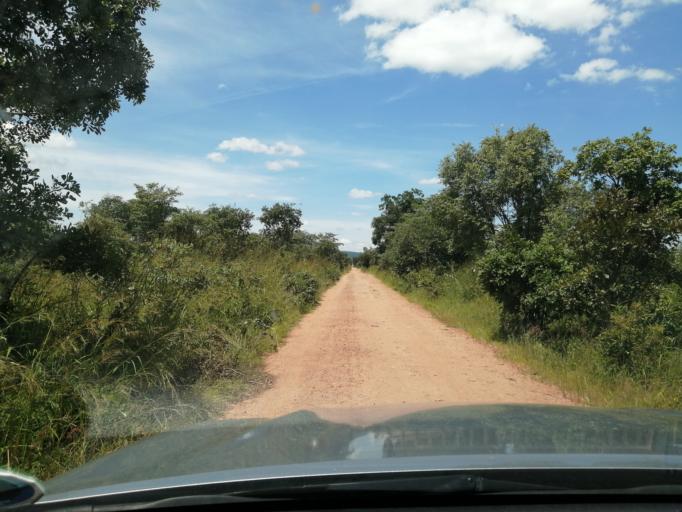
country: ZM
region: Central
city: Chibombo
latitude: -15.1216
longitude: 27.8621
